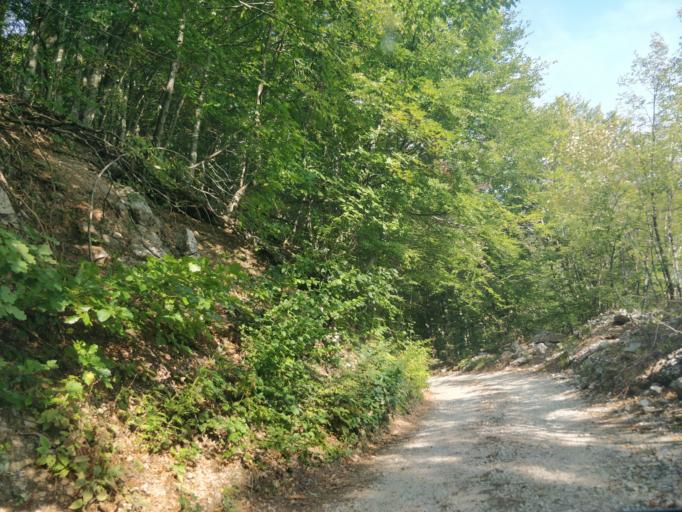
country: HR
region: Zadarska
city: Starigrad
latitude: 44.3772
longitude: 15.5421
